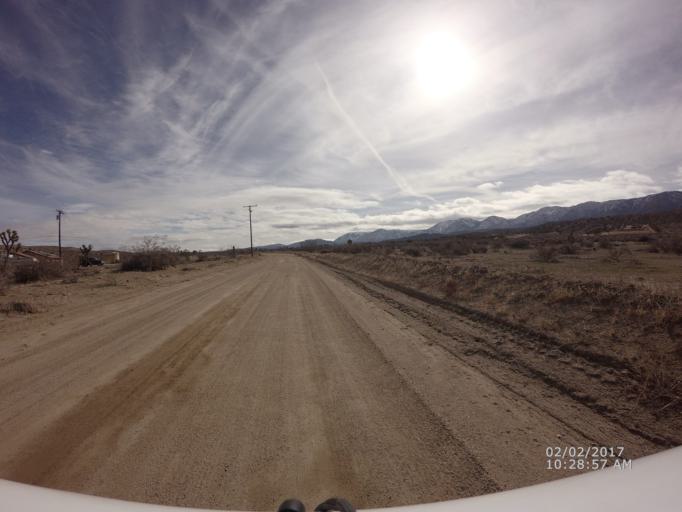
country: US
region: California
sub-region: Los Angeles County
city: Littlerock
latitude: 34.4870
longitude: -117.9344
